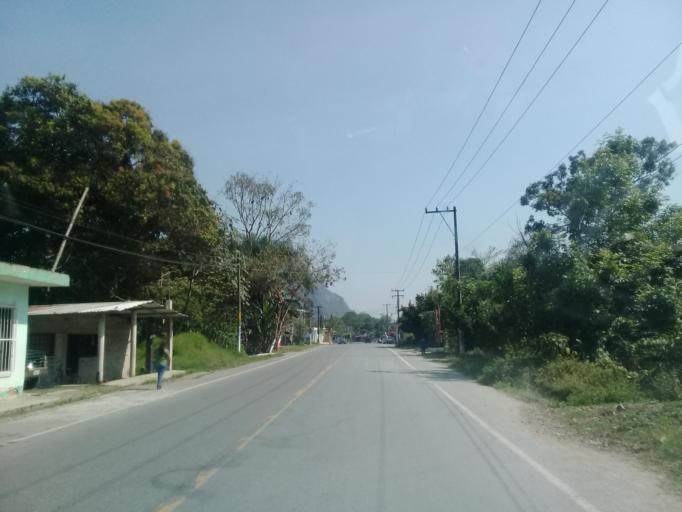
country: MX
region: Veracruz
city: Rafael Delgado
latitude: 18.7884
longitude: -97.0098
